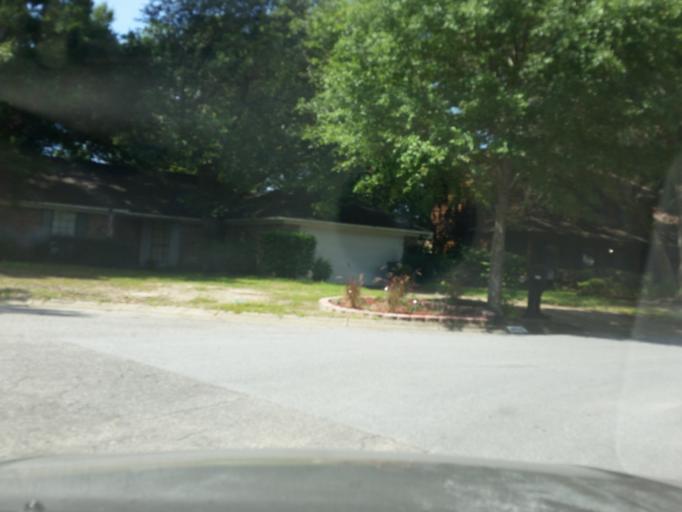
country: US
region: Florida
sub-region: Escambia County
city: Ferry Pass
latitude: 30.5213
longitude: -87.2046
